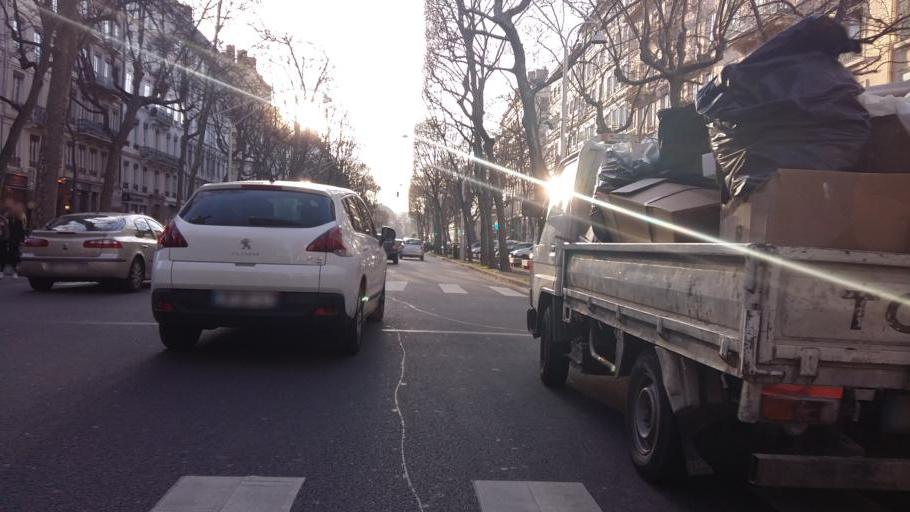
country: FR
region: Rhone-Alpes
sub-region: Departement du Rhone
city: Lyon
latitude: 45.7691
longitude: 4.8477
